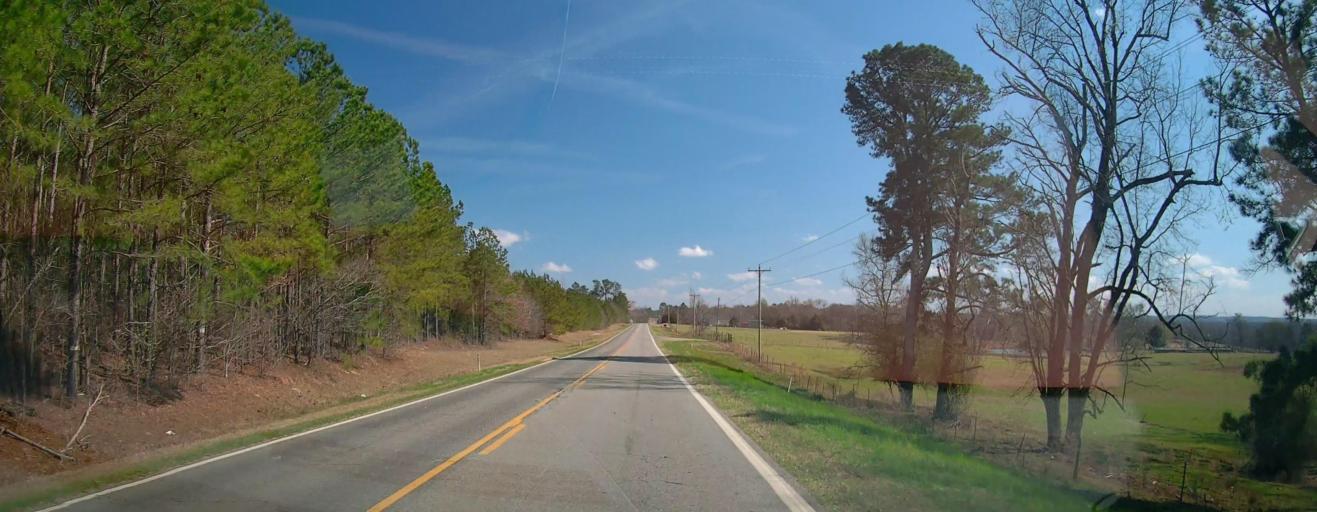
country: US
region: Georgia
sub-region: Wilkinson County
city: Gordon
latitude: 32.9278
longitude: -83.4028
